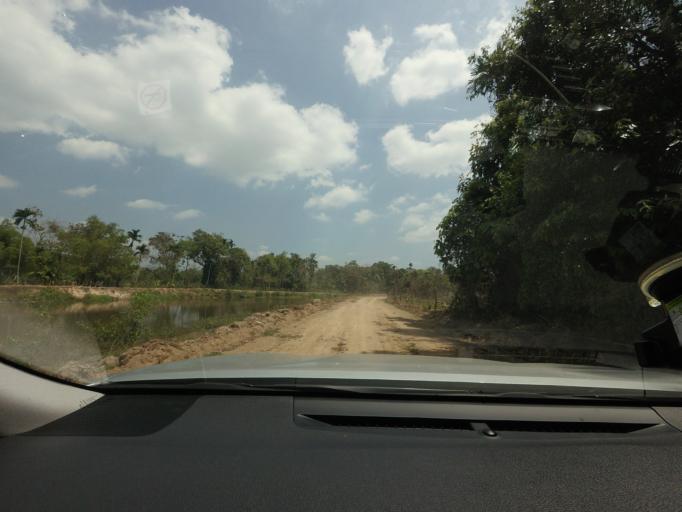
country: TH
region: Narathiwat
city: Rueso
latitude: 6.3902
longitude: 101.5003
